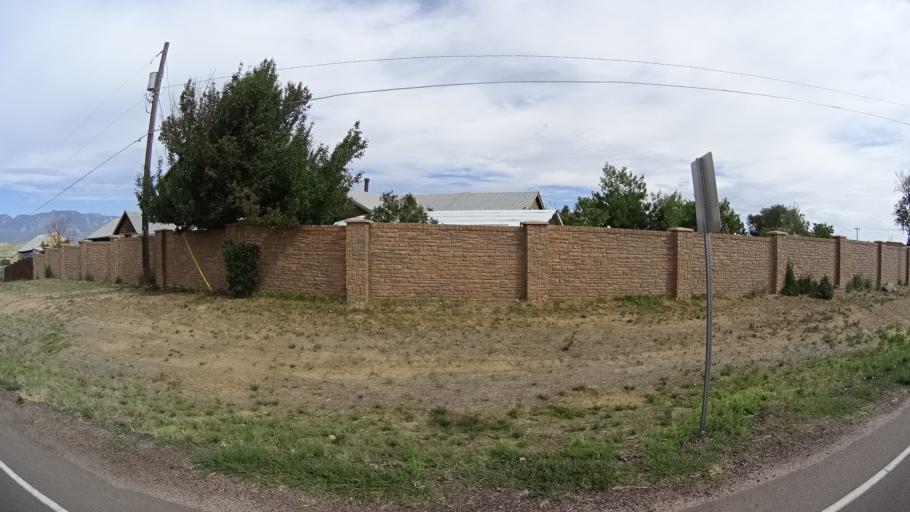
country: US
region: Colorado
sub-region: El Paso County
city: Fountain
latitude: 38.7083
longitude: -104.7020
